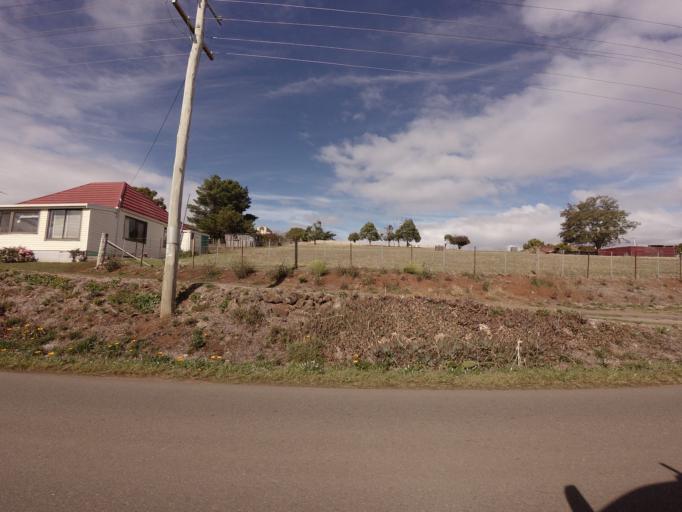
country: AU
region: Tasmania
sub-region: Derwent Valley
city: New Norfolk
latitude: -42.6995
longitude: 146.9189
